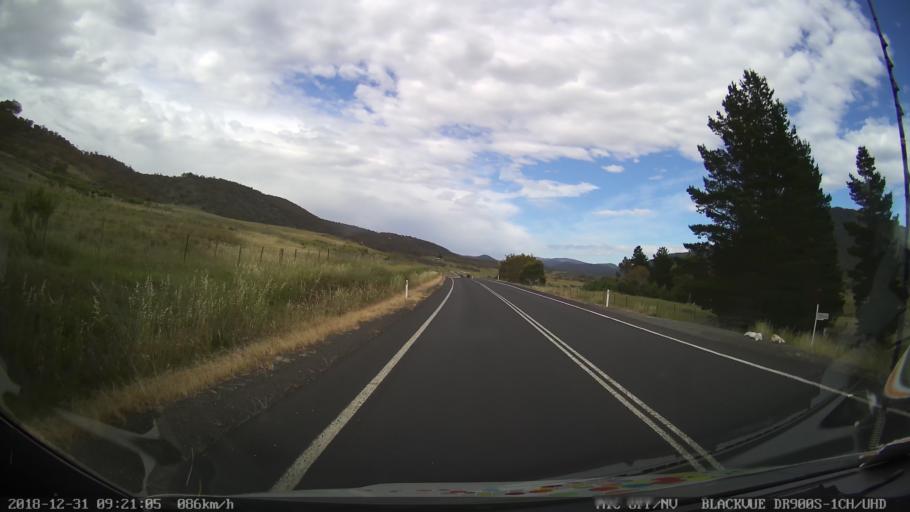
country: AU
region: New South Wales
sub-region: Snowy River
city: Jindabyne
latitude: -36.4261
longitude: 148.5662
